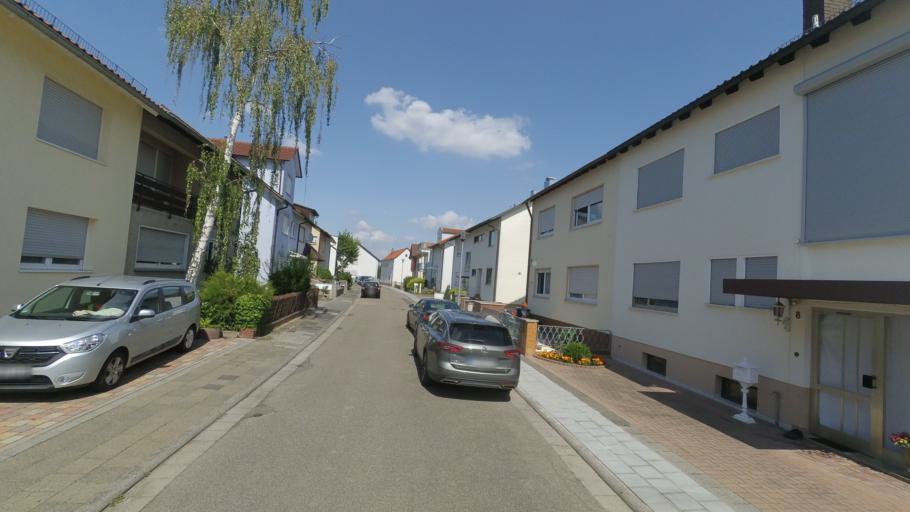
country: DE
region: Rheinland-Pfalz
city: Schifferstadt
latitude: 49.3794
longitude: 8.3793
